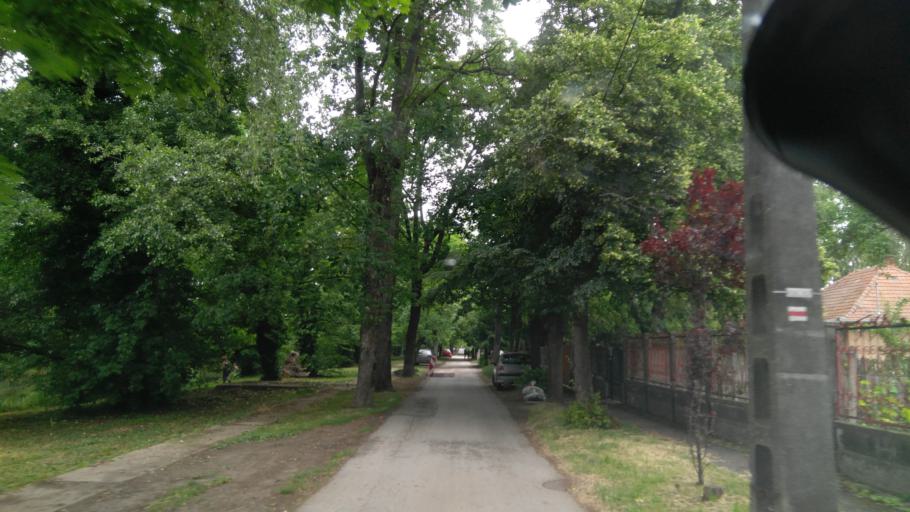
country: HU
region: Bekes
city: Bekescsaba
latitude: 46.6883
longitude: 21.0983
